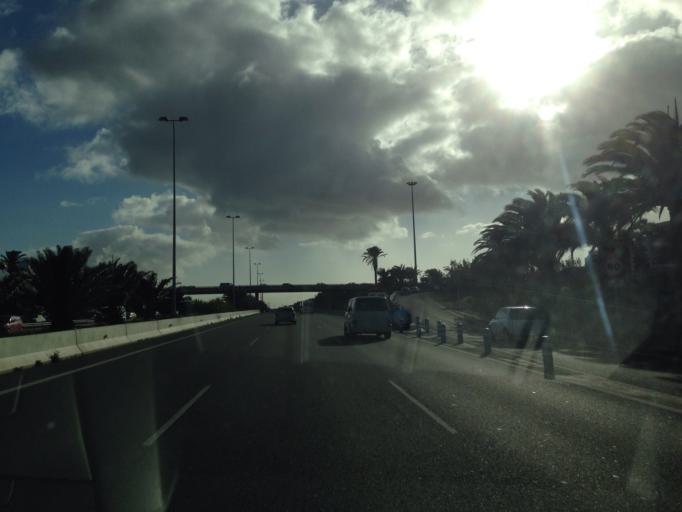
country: ES
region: Canary Islands
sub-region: Provincia de Las Palmas
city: Cruce de Arinaga
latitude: 27.8421
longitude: -15.4385
